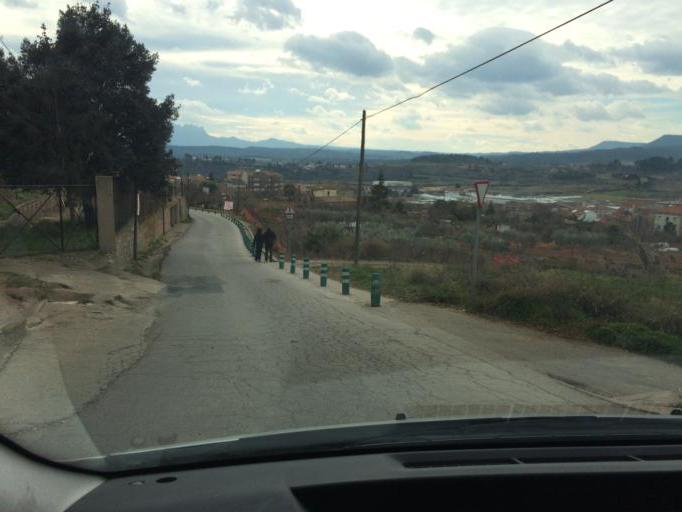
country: ES
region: Catalonia
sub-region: Provincia de Barcelona
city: Manresa
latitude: 41.7349
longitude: 1.8167
